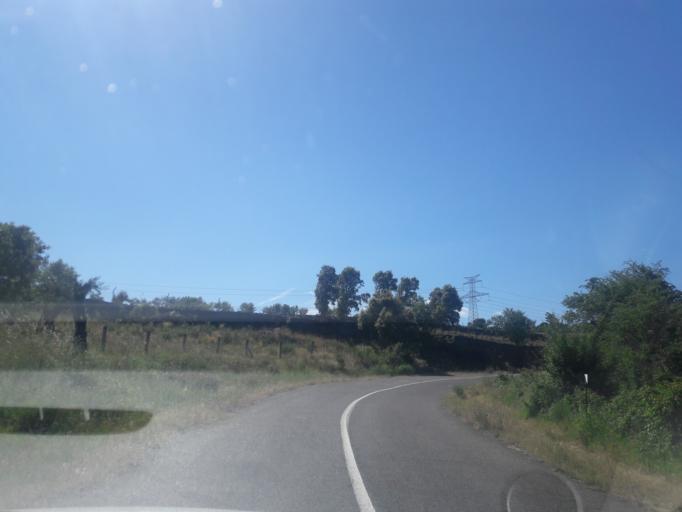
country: ES
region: Castille and Leon
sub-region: Provincia de Salamanca
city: Saucelle
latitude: 41.0053
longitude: -6.7347
